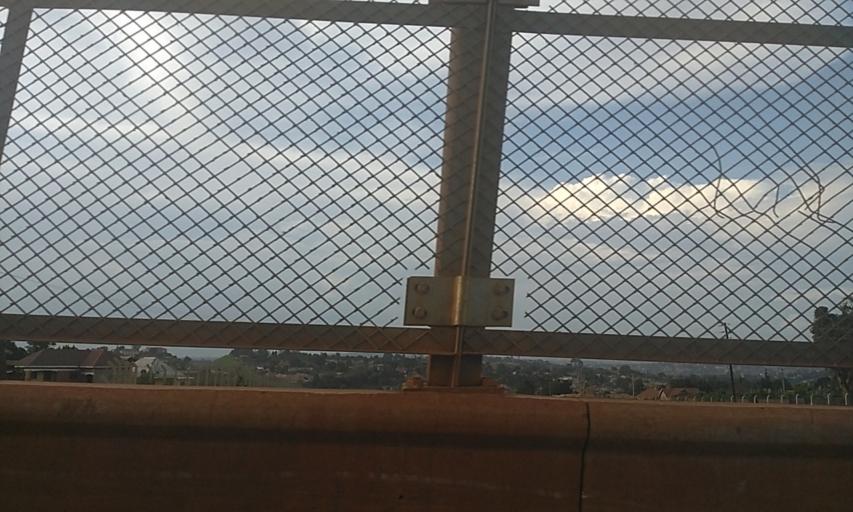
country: UG
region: Central Region
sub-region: Wakiso District
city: Kajansi
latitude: 0.2710
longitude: 32.5199
